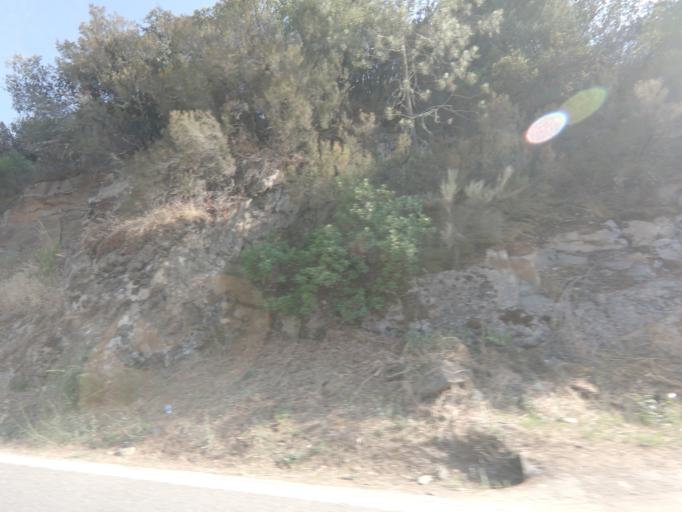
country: PT
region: Viseu
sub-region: Tabuaco
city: Tabuaco
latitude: 41.1446
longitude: -7.5764
